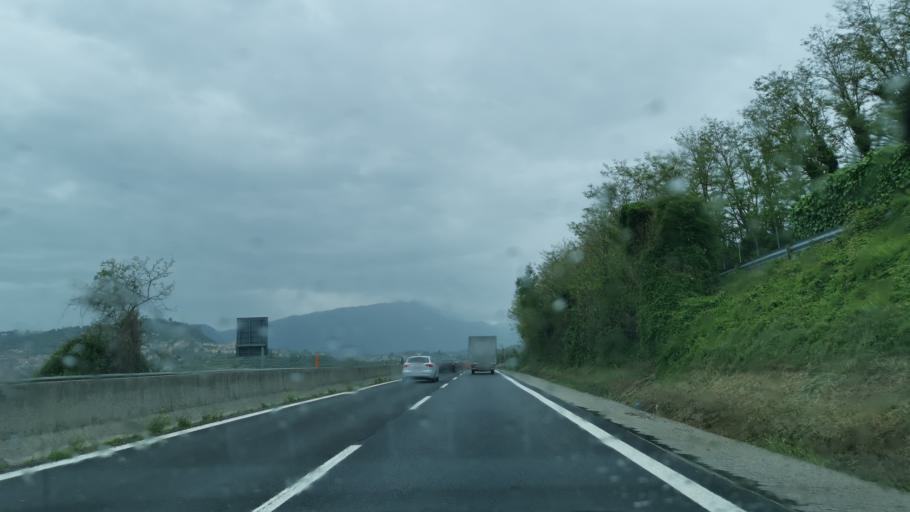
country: IT
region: Veneto
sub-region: Provincia di Verona
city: Calmasino
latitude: 45.5203
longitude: 10.7707
